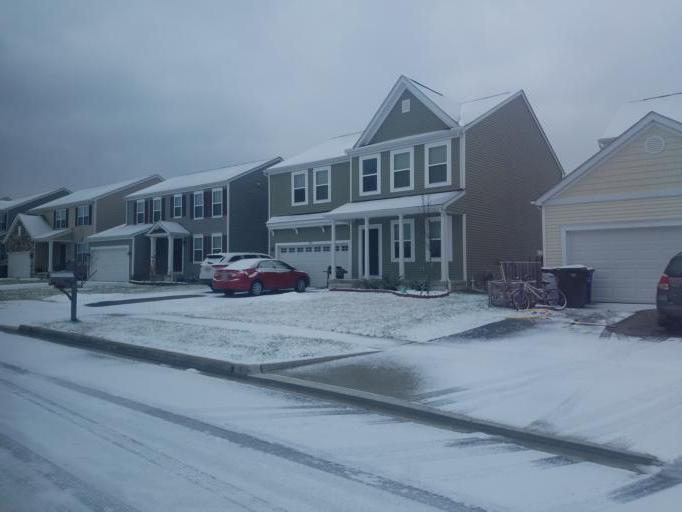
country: US
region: Ohio
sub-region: Franklin County
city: Reynoldsburg
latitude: 39.9965
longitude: -82.7978
